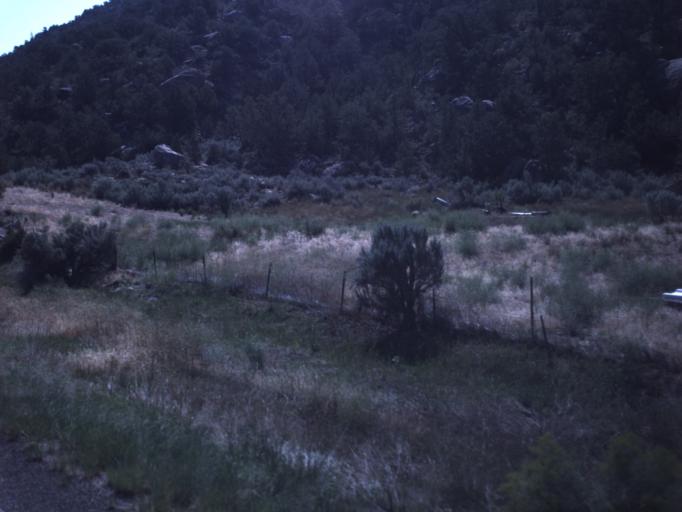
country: US
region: Utah
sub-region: Duchesne County
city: Duchesne
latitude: 40.2975
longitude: -110.5396
